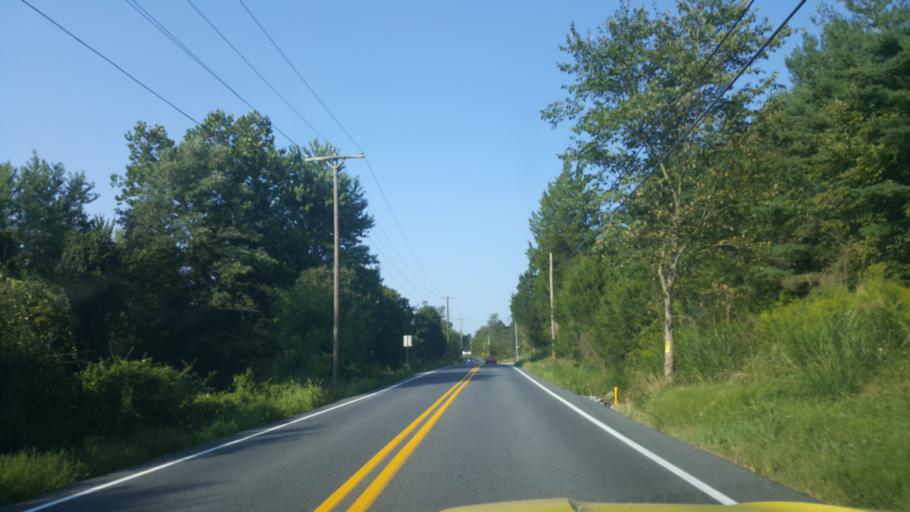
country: US
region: Pennsylvania
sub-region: Lebanon County
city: Campbelltown
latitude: 40.2253
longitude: -76.5359
